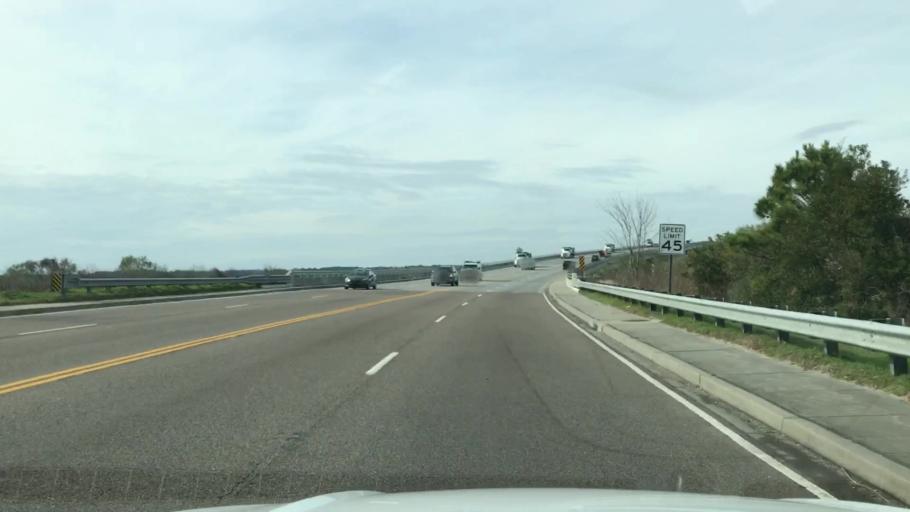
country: US
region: South Carolina
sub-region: Charleston County
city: Charleston
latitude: 32.7538
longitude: -80.0030
